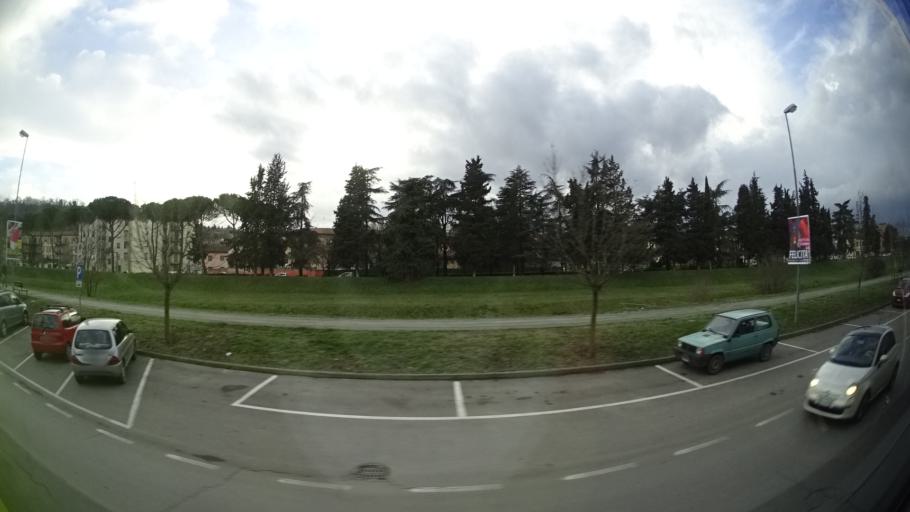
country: IT
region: Tuscany
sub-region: Provincia di Siena
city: Poggibonsi
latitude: 43.4692
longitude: 11.1528
